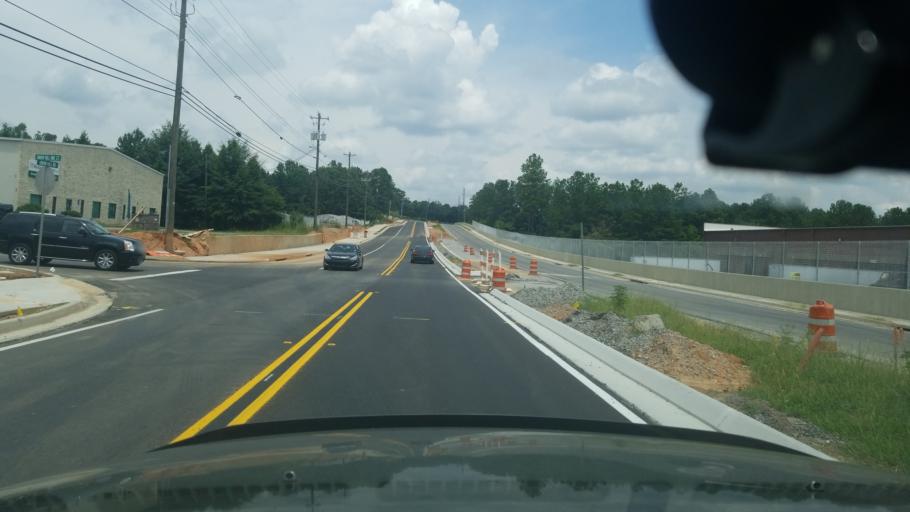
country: US
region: Georgia
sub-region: Fulton County
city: Milton
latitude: 34.1141
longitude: -84.2368
